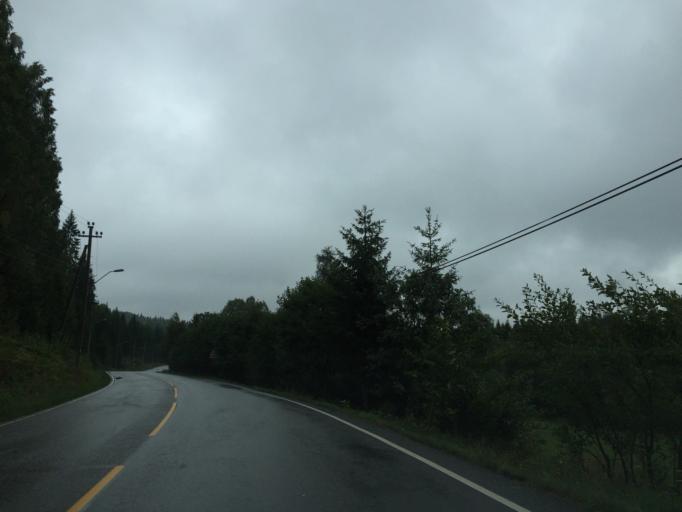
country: NO
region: Akershus
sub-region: Baerum
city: Lysaker
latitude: 59.9969
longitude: 10.6203
